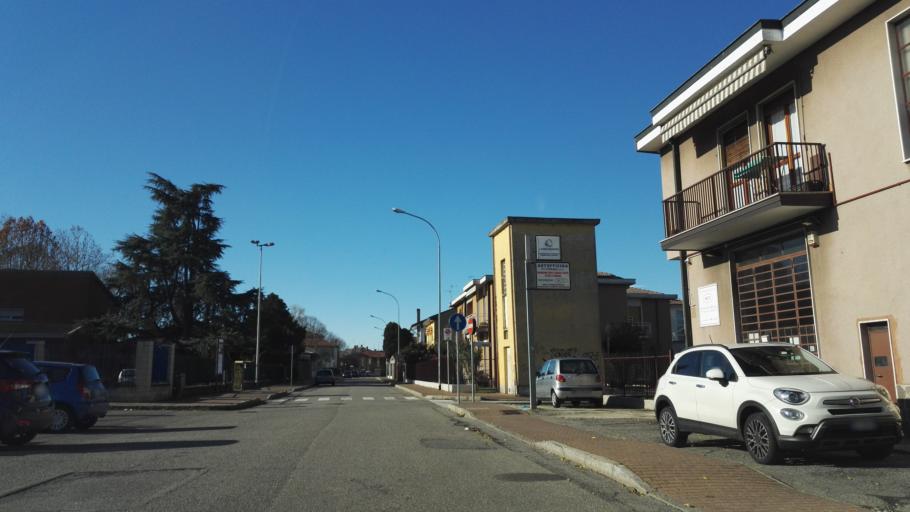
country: IT
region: Lombardy
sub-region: Citta metropolitana di Milano
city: Civesio
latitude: 45.3939
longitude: 9.2481
